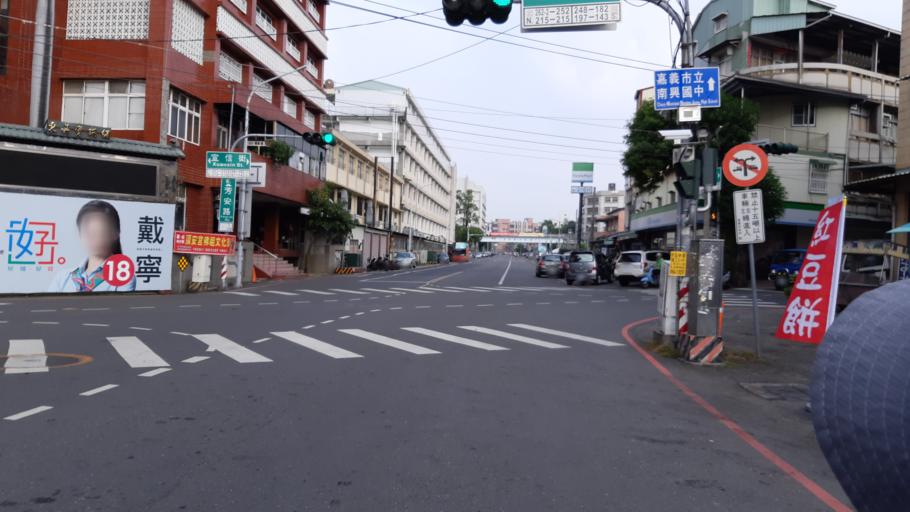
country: TW
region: Taiwan
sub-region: Chiayi
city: Jiayi Shi
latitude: 23.4685
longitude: 120.4603
